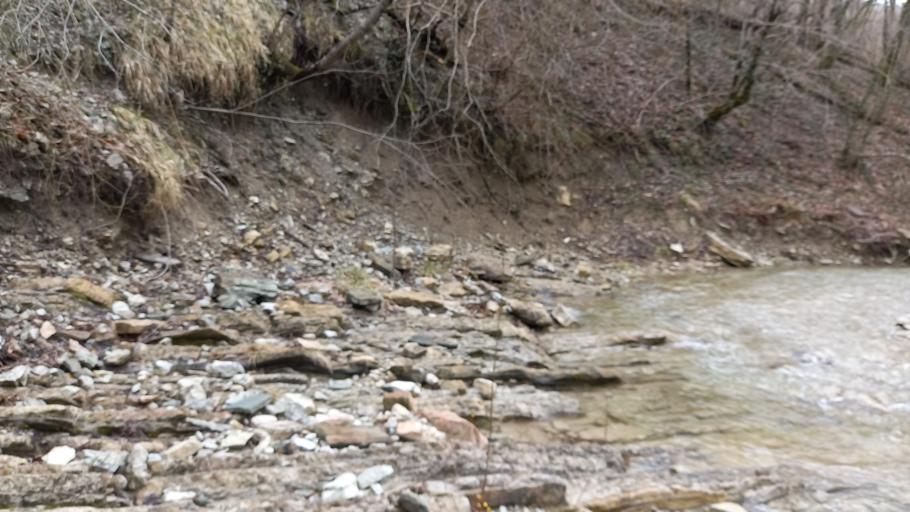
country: RU
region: Krasnodarskiy
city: Dzhubga
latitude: 44.4041
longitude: 38.7091
